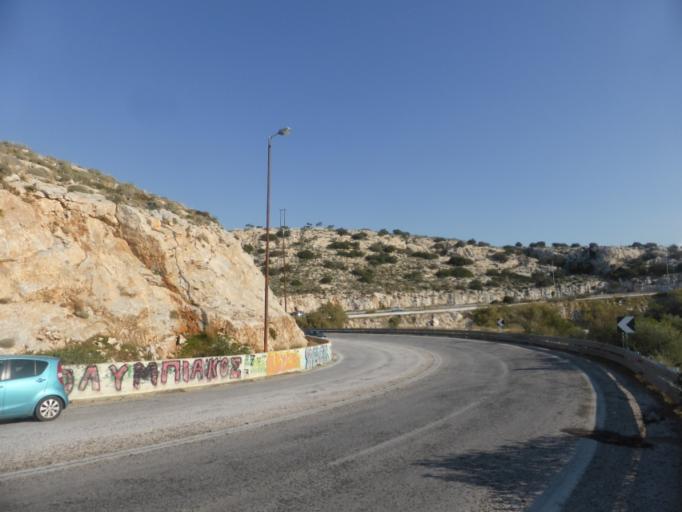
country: GR
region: Attica
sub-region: Nomarchia Anatolikis Attikis
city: Vouliagmeni
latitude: 37.8026
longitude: 23.7851
